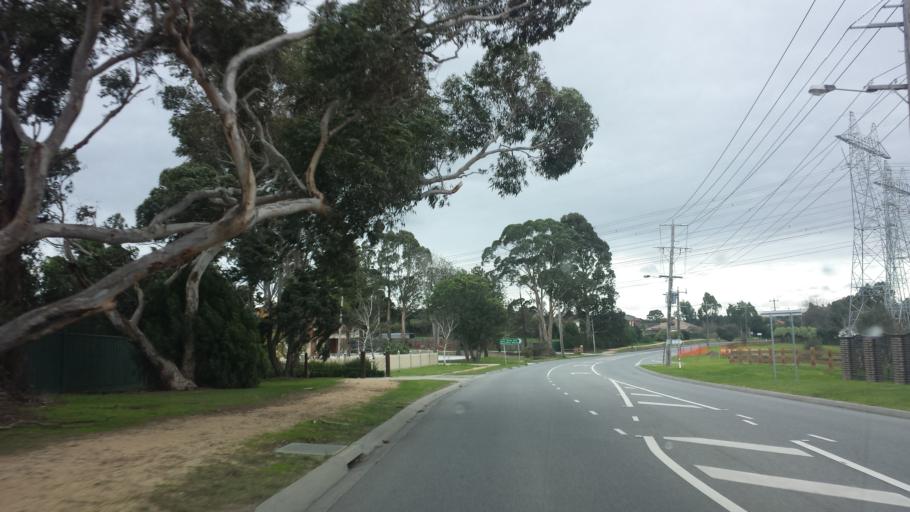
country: AU
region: Victoria
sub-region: Casey
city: Narre Warren North
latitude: -37.9908
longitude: 145.2914
